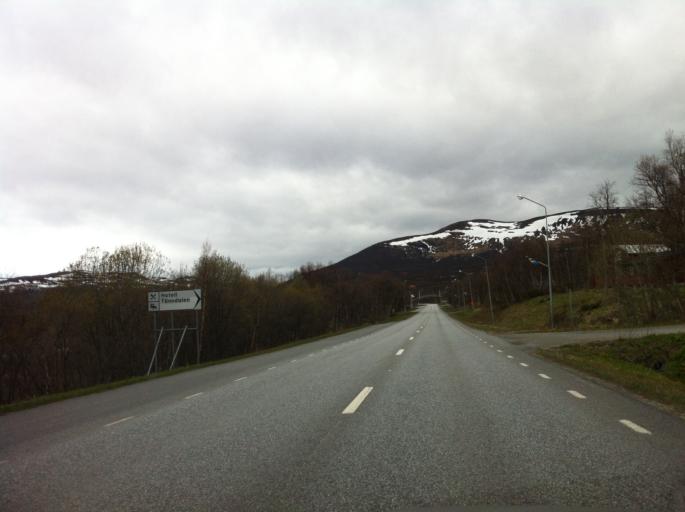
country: NO
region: Sor-Trondelag
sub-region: Tydal
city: Aas
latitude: 62.5411
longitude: 12.3379
